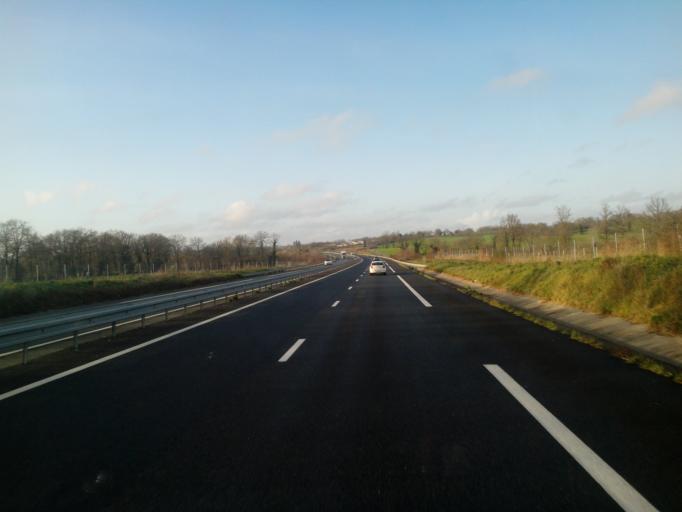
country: FR
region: Poitou-Charentes
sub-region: Departement des Deux-Sevres
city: Saint-Pierre-des-Echaubrognes
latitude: 46.9572
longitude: -0.7795
